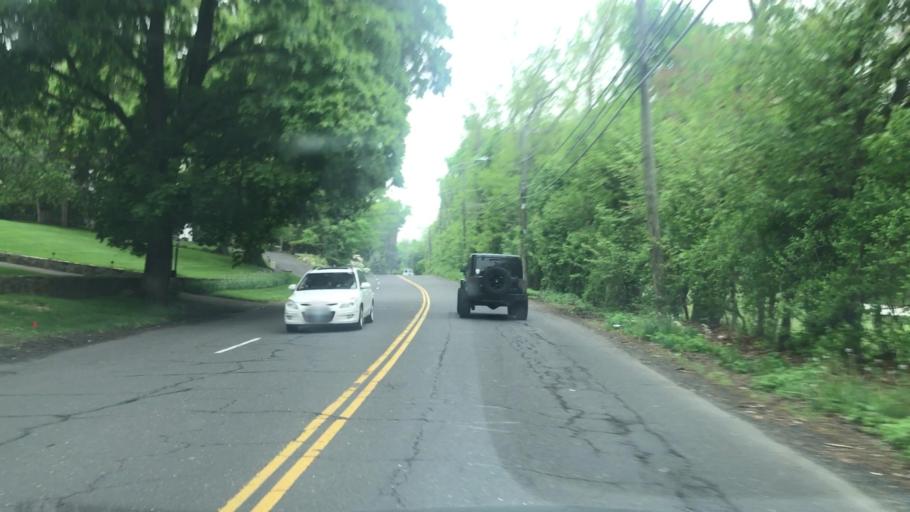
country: US
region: Connecticut
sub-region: Fairfield County
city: Stamford
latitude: 41.0609
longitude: -73.5591
